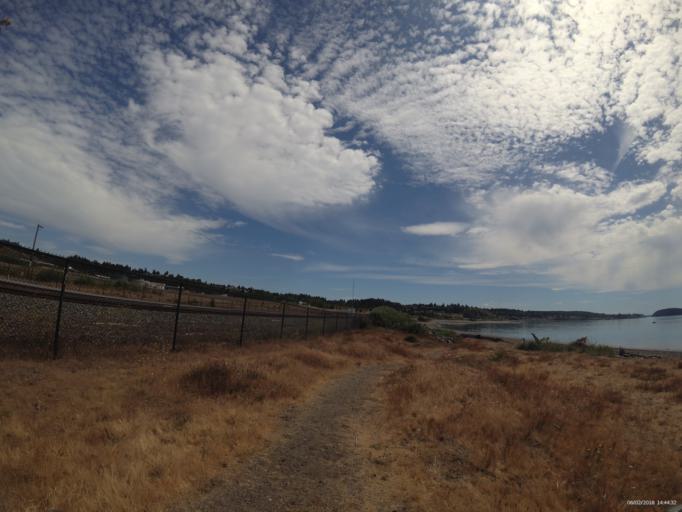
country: US
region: Washington
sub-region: Pierce County
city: Steilacoom
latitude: 47.1976
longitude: -122.5826
